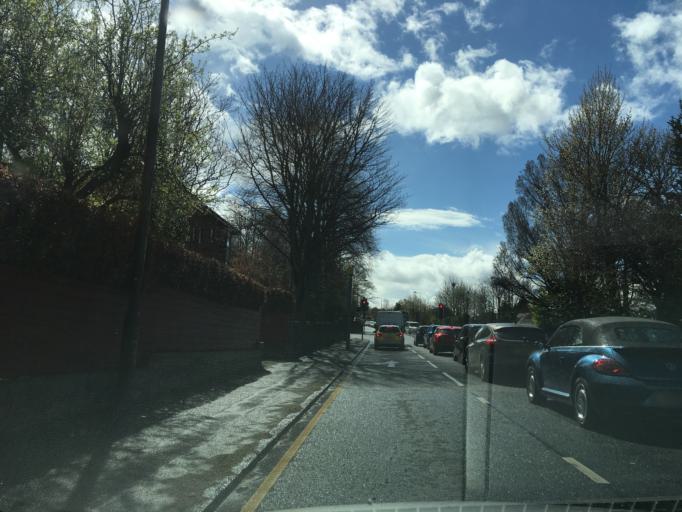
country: GB
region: Scotland
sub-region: Edinburgh
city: Colinton
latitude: 55.9207
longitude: -3.2393
